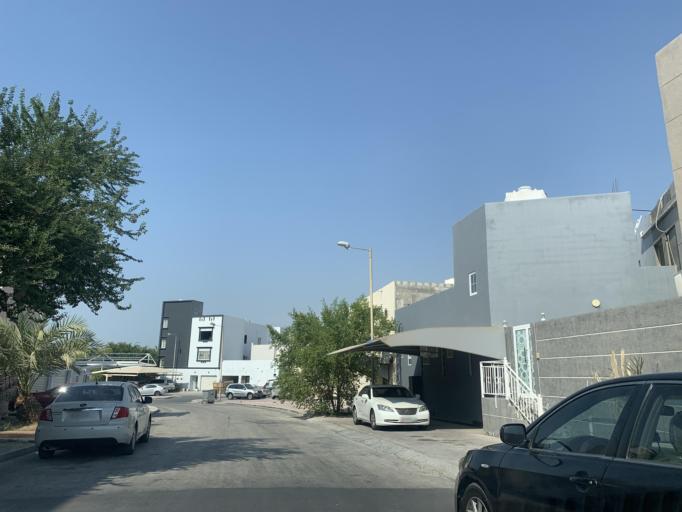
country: BH
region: Central Governorate
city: Madinat Hamad
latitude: 26.1094
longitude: 50.5012
